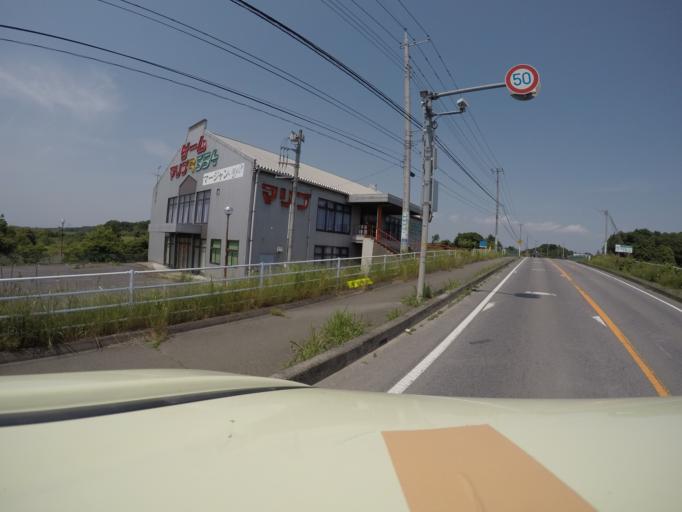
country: JP
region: Ibaraki
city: Iwai
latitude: 36.0343
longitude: 139.9098
